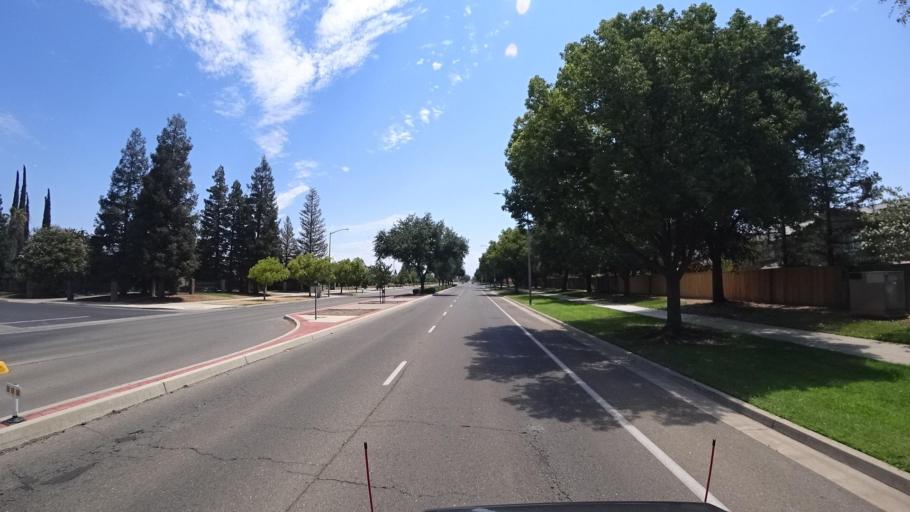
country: US
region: California
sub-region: Fresno County
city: Tarpey Village
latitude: 36.7939
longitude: -119.6678
